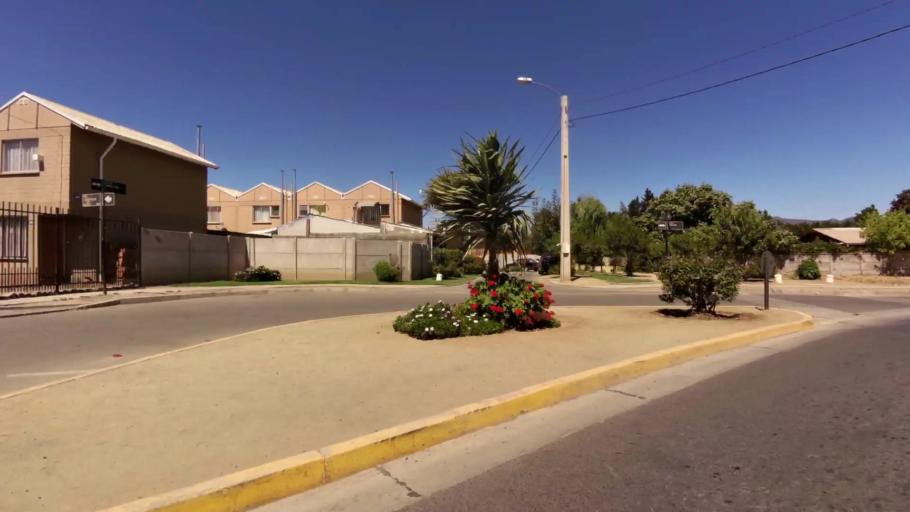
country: CL
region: O'Higgins
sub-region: Provincia de Cachapoal
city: Rancagua
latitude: -34.1743
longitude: -70.7828
